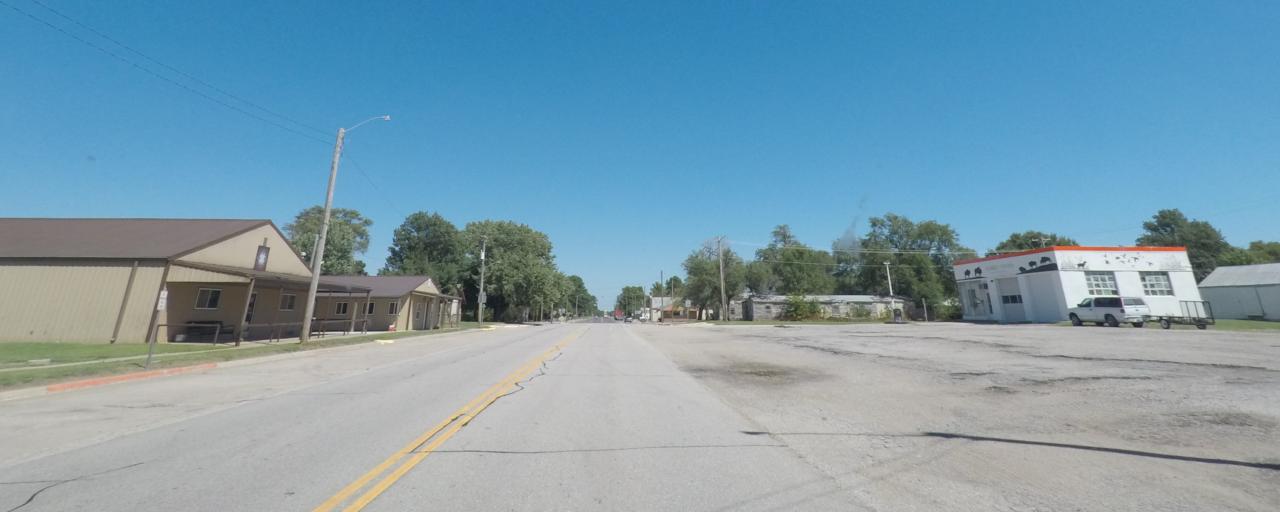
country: US
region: Kansas
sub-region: Sumner County
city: Caldwell
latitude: 37.0479
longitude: -97.4011
